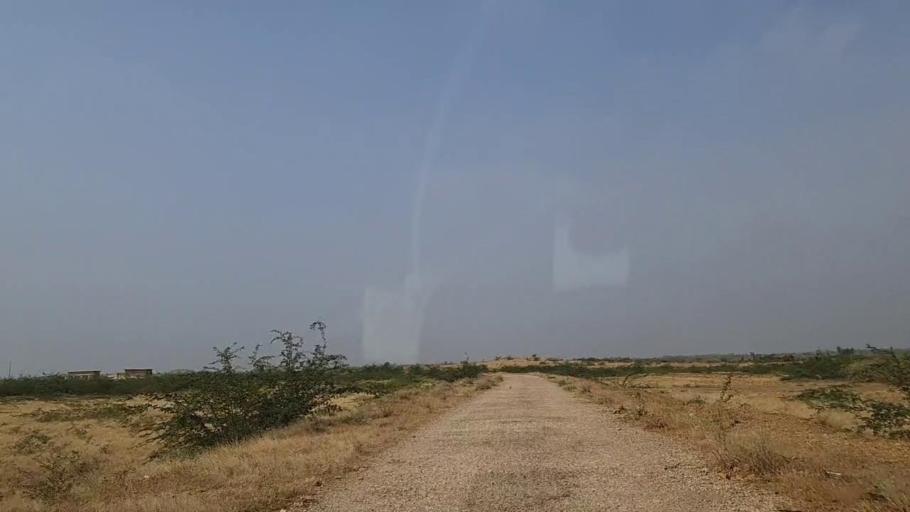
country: PK
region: Sindh
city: Thatta
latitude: 24.7207
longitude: 67.8285
